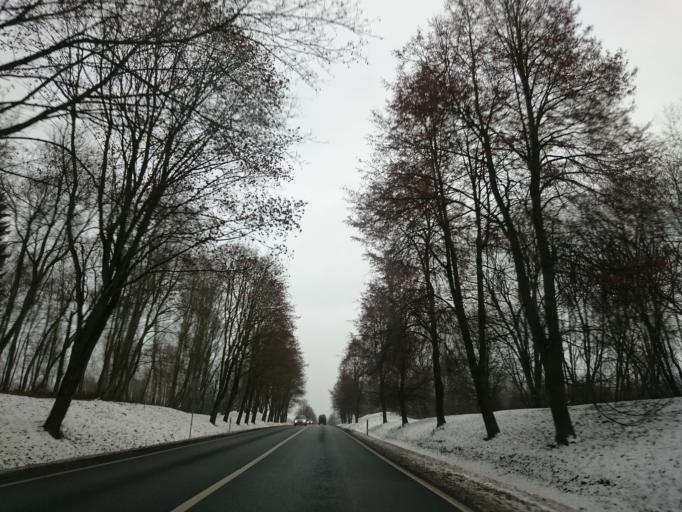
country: LV
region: Krimulda
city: Ragana
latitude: 57.1679
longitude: 24.7008
